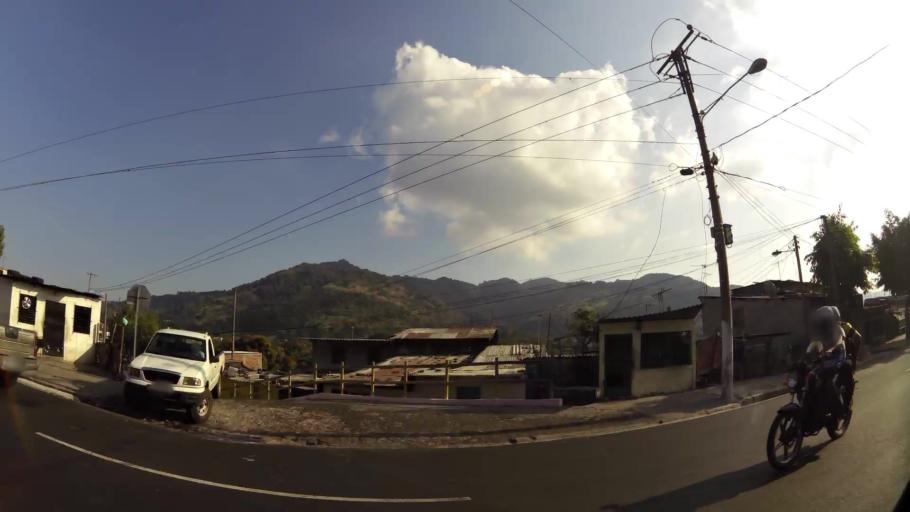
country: SV
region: San Salvador
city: San Salvador
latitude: 13.6960
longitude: -89.1760
